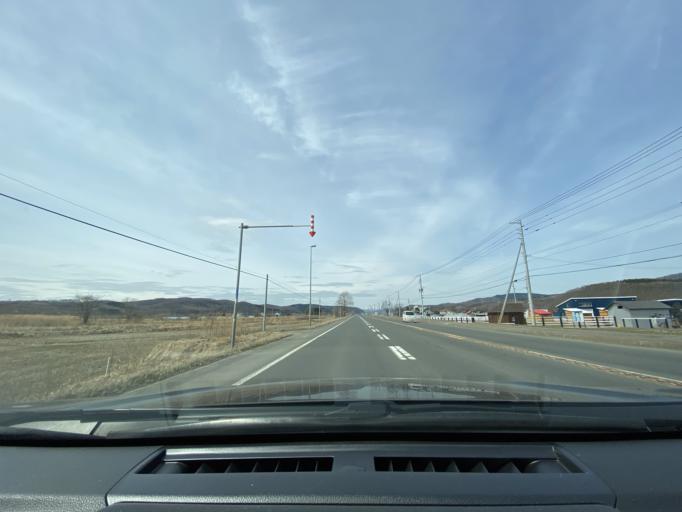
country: JP
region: Hokkaido
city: Kitami
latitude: 43.7941
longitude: 143.7241
